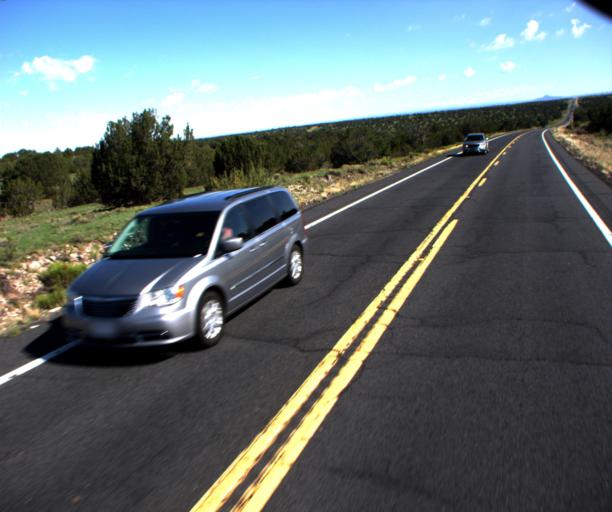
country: US
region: Arizona
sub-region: Coconino County
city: Williams
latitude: 35.5090
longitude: -112.1731
